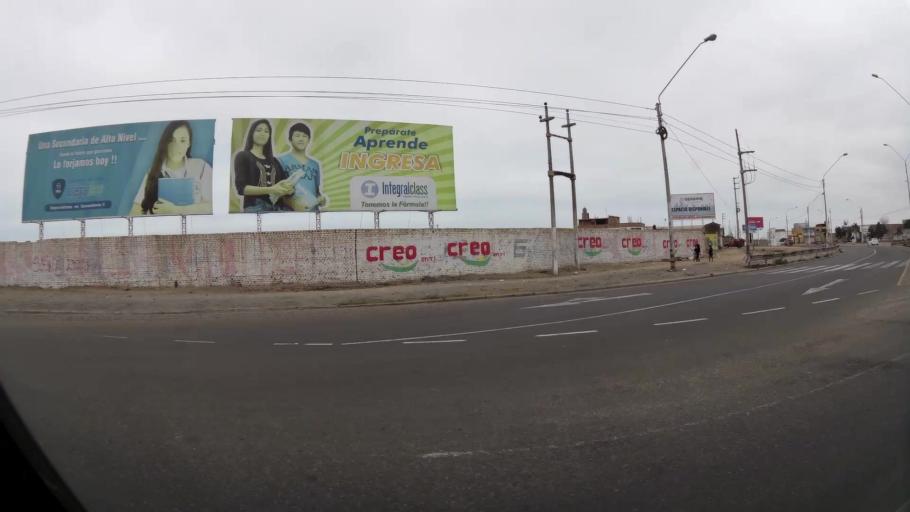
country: PE
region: La Libertad
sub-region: Provincia de Trujillo
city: Huanchaco
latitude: -8.0875
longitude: -79.0970
